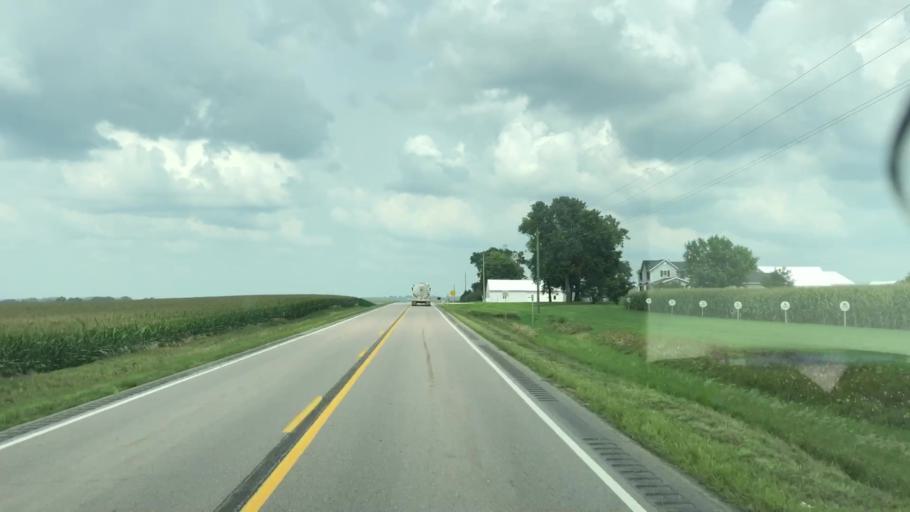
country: US
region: Iowa
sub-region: Plymouth County
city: Remsen
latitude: 42.8024
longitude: -95.9577
